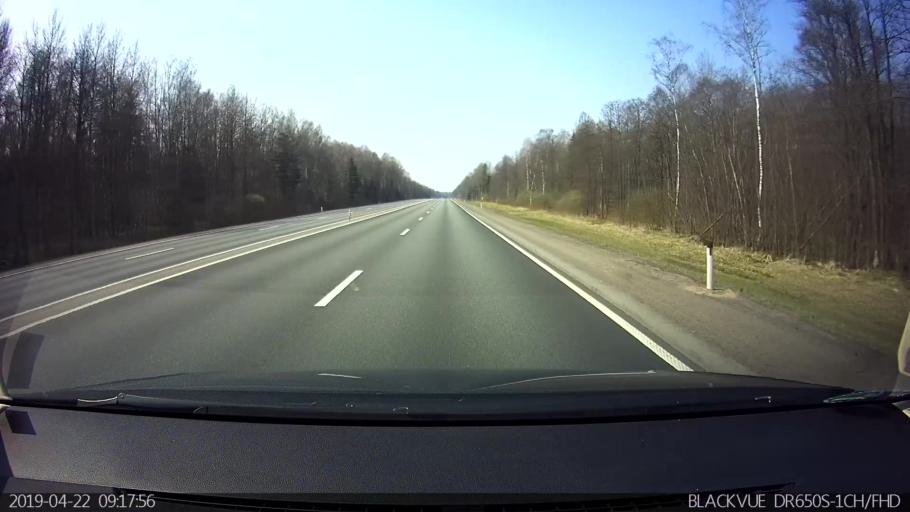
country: RU
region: Smolensk
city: Golynki
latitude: 54.7586
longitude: 31.5038
